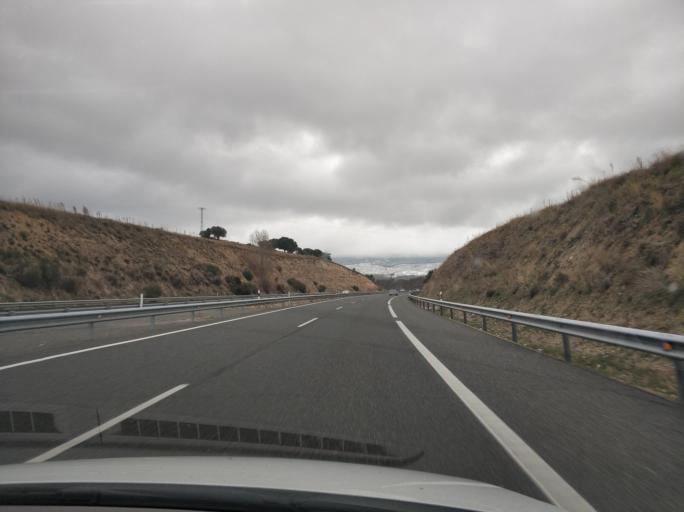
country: ES
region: Castille and Leon
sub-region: Provincia de Segovia
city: Cerezo de Abajo
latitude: 41.2199
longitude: -3.5844
